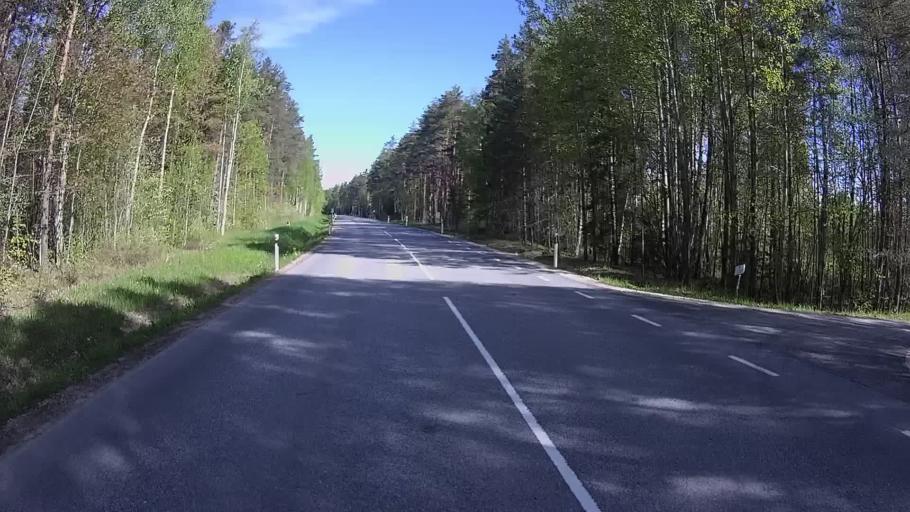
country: EE
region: Polvamaa
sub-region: Raepina vald
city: Rapina
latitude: 58.0351
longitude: 27.5681
